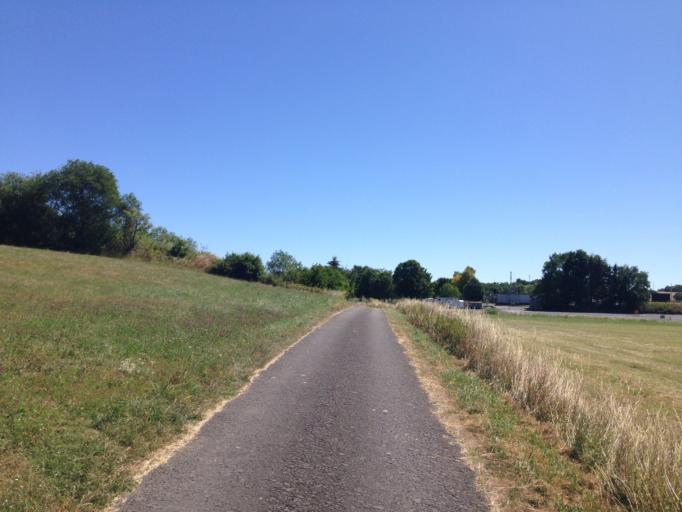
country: DE
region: Hesse
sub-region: Regierungsbezirk Giessen
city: Reiskirchen
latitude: 50.5874
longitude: 8.8152
